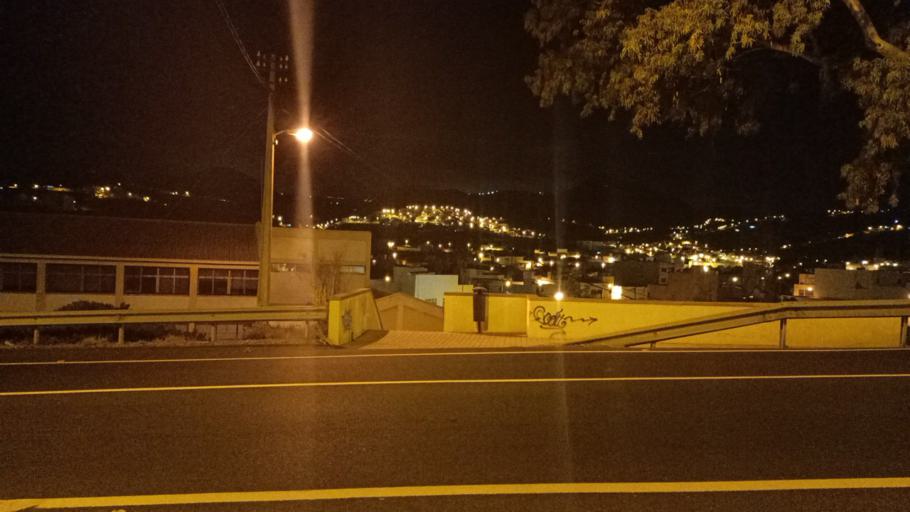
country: ES
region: Canary Islands
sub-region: Provincia de Las Palmas
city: Telde
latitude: 28.0412
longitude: -15.4191
